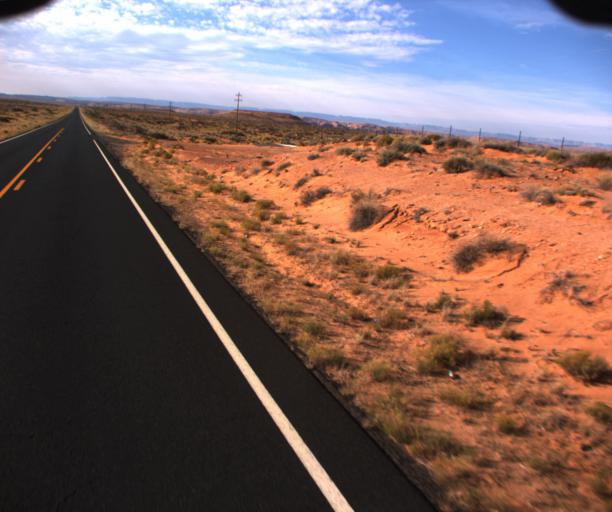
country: US
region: Arizona
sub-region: Apache County
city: Many Farms
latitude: 36.8549
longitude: -109.6372
